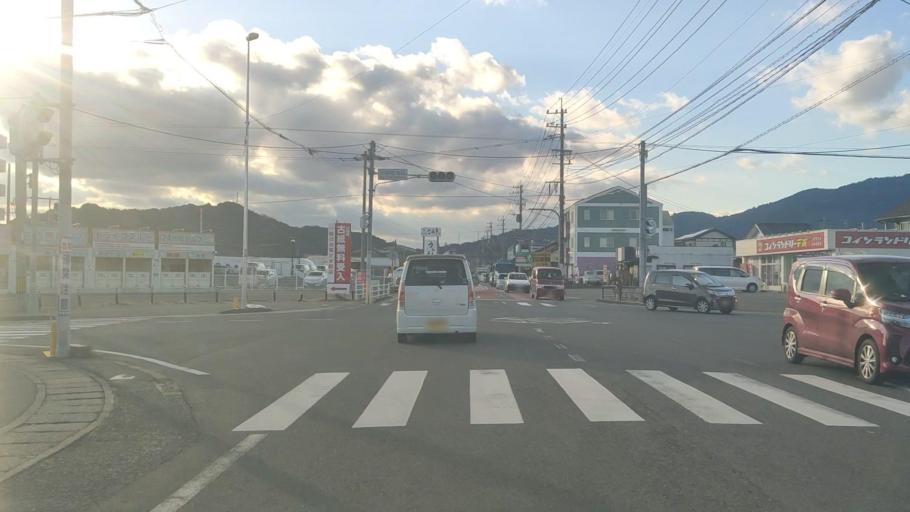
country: JP
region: Saga Prefecture
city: Saga-shi
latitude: 33.2929
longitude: 130.1899
